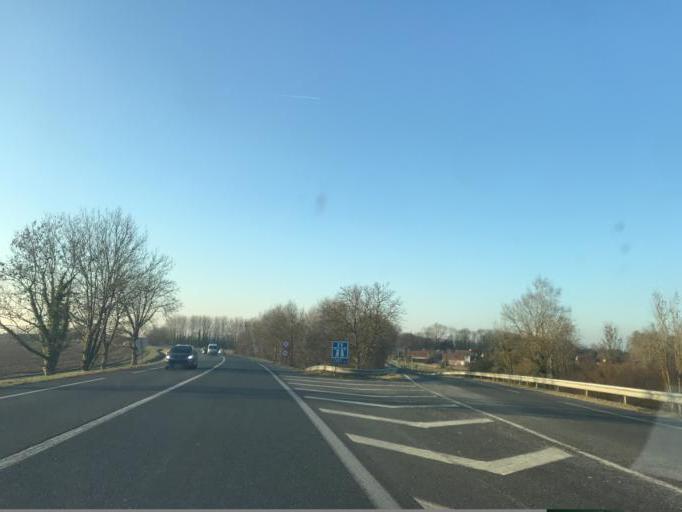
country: FR
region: Ile-de-France
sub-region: Departement de Seine-et-Marne
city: Villiers-sur-Morin
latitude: 48.8524
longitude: 2.8625
